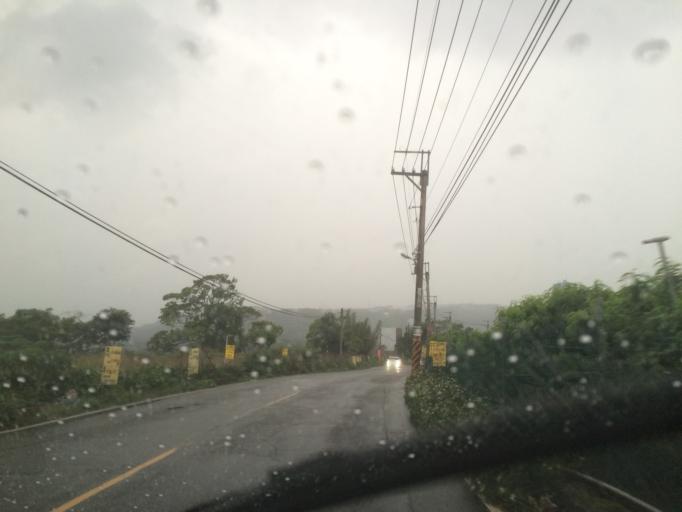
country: TW
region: Taiwan
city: Fengyuan
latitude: 24.2013
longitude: 120.7987
